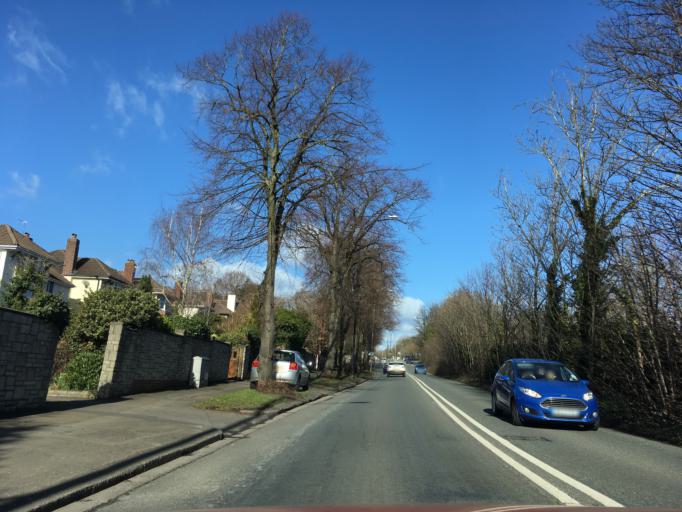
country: GB
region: England
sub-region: Bristol
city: Bristol
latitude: 51.5004
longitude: -2.6167
